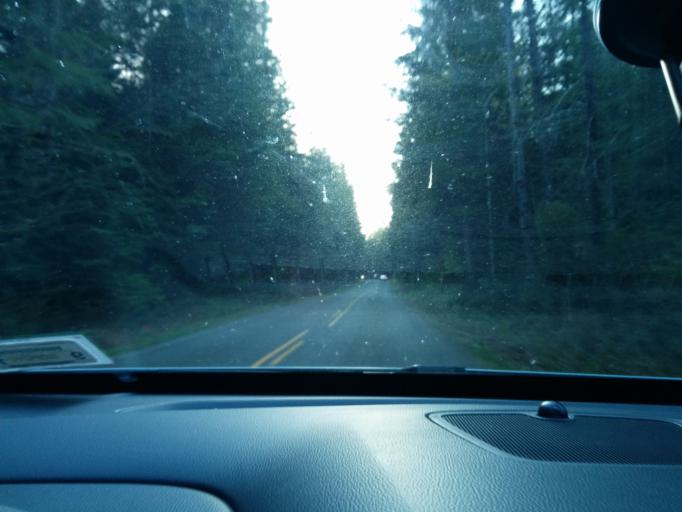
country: US
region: Washington
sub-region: Snohomish County
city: Gold Bar
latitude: 47.8948
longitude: -121.7421
